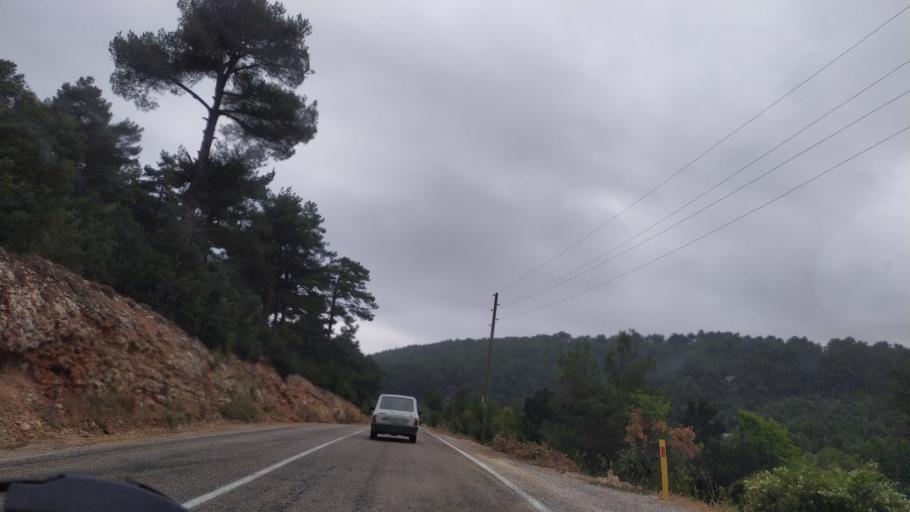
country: TR
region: Mersin
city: Silifke
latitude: 36.5381
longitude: 33.9416
